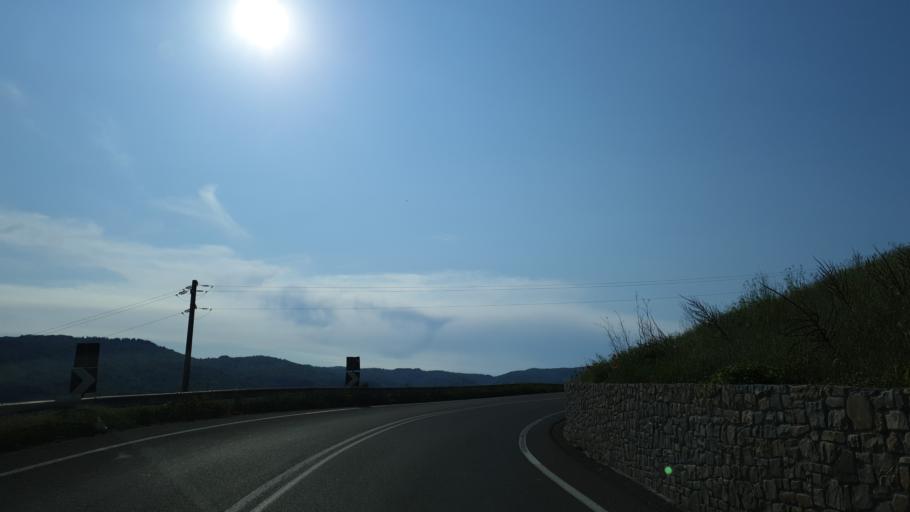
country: IT
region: Tuscany
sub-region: Province of Arezzo
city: Strada
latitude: 43.7555
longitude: 11.7184
